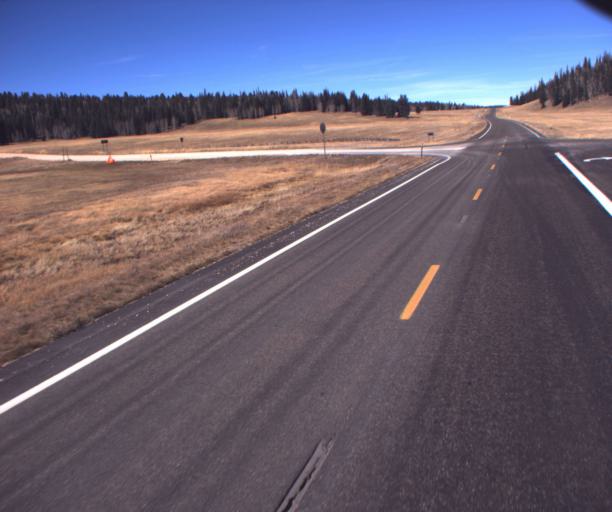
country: US
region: Arizona
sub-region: Coconino County
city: Grand Canyon
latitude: 36.4006
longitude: -112.1293
